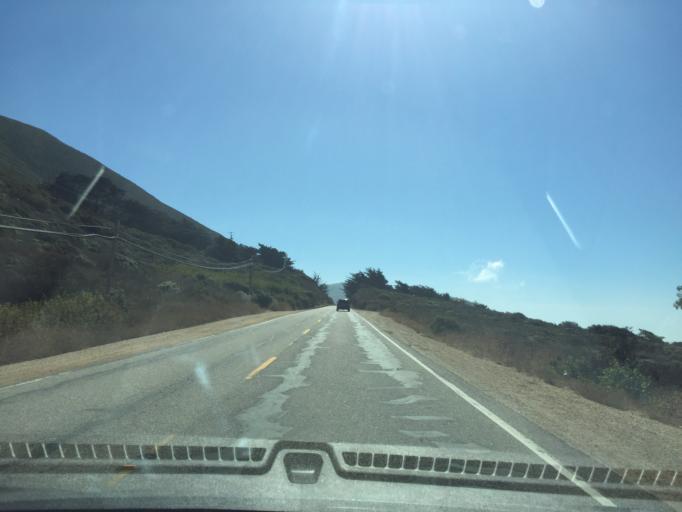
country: US
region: California
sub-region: Monterey County
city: Carmel-by-the-Sea
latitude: 36.3956
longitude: -121.9028
